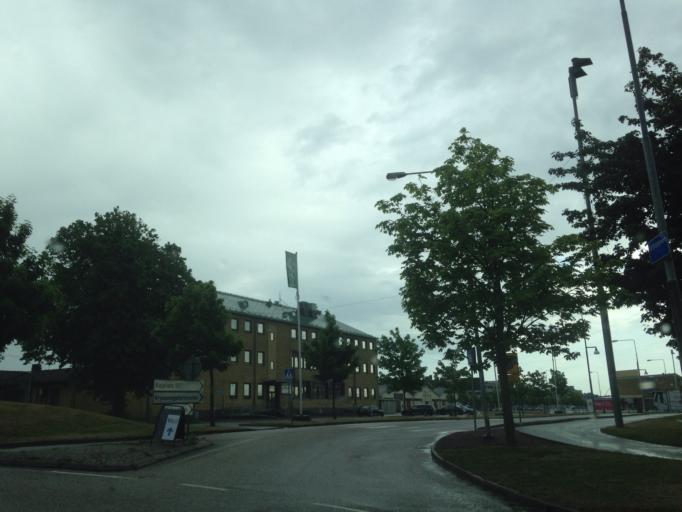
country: SE
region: Vaestra Goetaland
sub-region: Goteborg
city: Goeteborg
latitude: 57.7193
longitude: 11.9605
